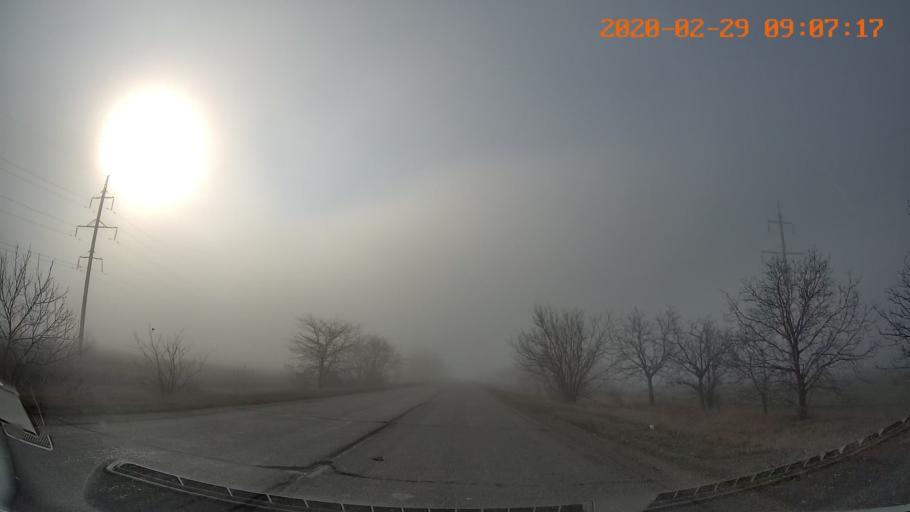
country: MD
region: Telenesti
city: Tiraspolul Nou
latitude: 46.8642
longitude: 29.7482
